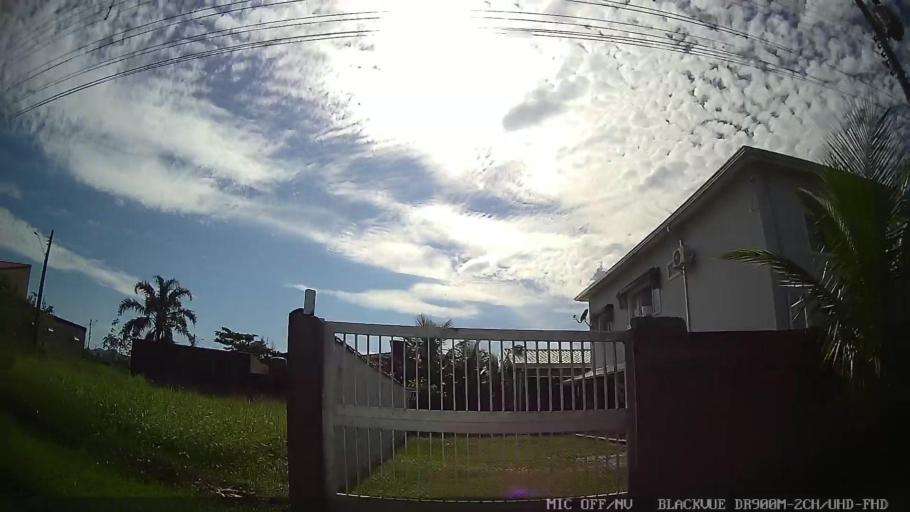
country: BR
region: Sao Paulo
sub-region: Iguape
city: Iguape
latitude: -24.7725
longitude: -47.5914
